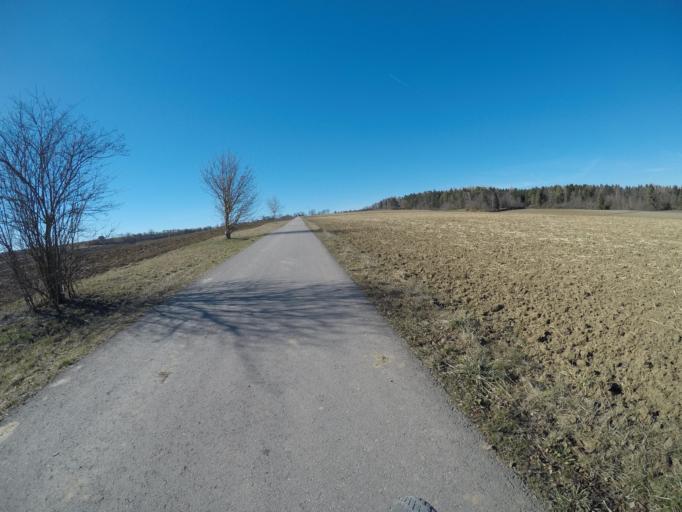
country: DE
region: Baden-Wuerttemberg
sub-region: Regierungsbezirk Stuttgart
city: Herrenberg
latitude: 48.5677
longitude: 8.8648
